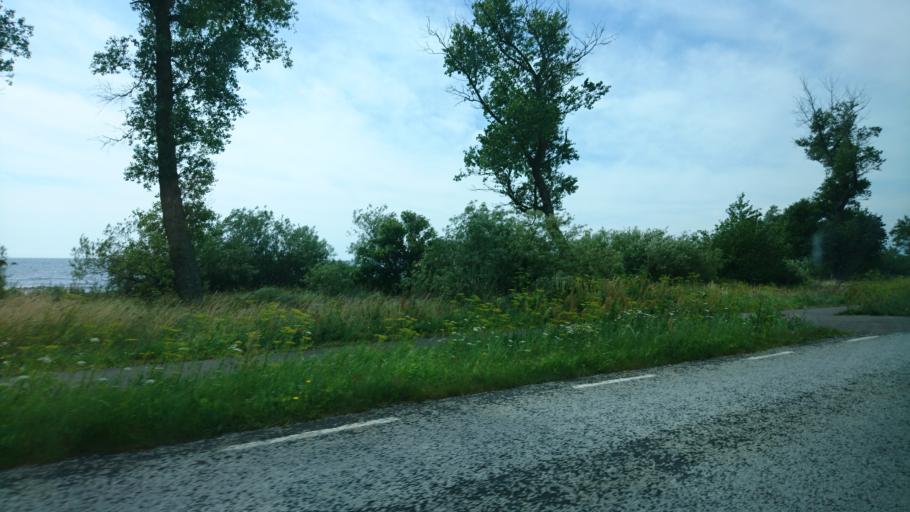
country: SE
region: Skane
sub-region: Skurups Kommun
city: Skivarp
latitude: 55.3881
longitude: 13.5394
